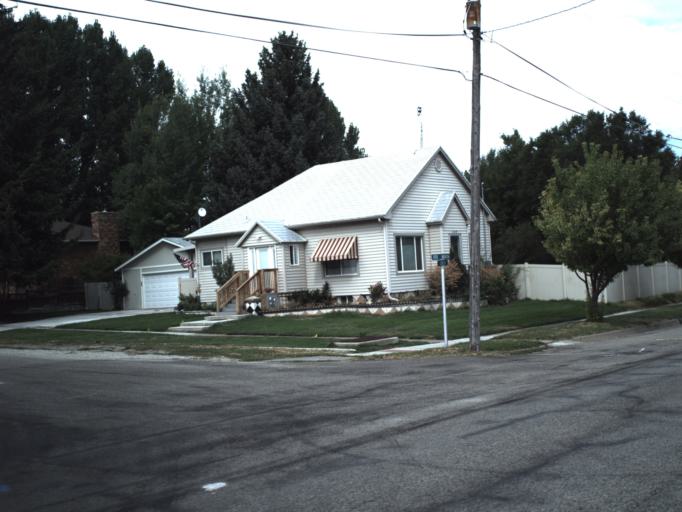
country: US
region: Utah
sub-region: Cache County
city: Wellsville
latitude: 41.6407
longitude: -111.9343
